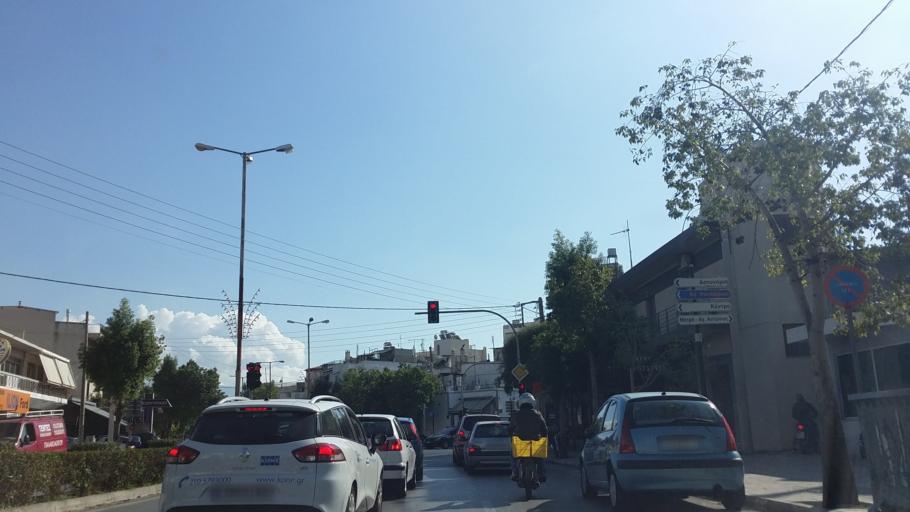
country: GR
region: Attica
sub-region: Nomarchia Athinas
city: Ilion
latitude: 38.0194
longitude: 23.7087
